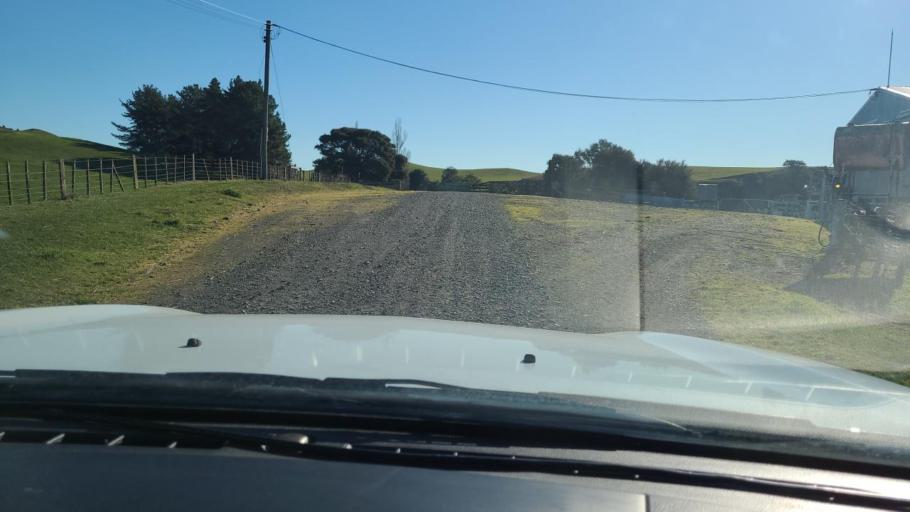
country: NZ
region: Hawke's Bay
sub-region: Napier City
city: Taradale
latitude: -39.4580
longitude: 176.6286
